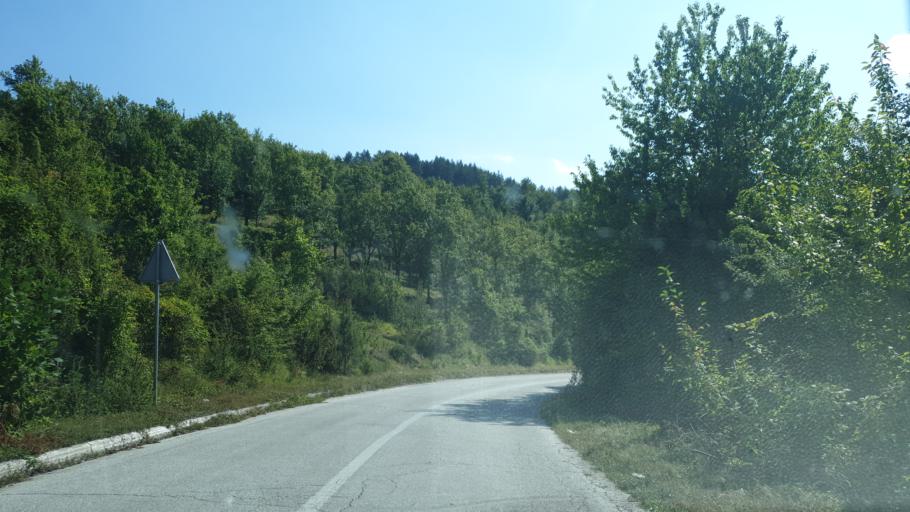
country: RS
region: Central Serbia
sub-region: Zlatiborski Okrug
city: Cajetina
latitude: 43.6823
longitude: 19.8509
